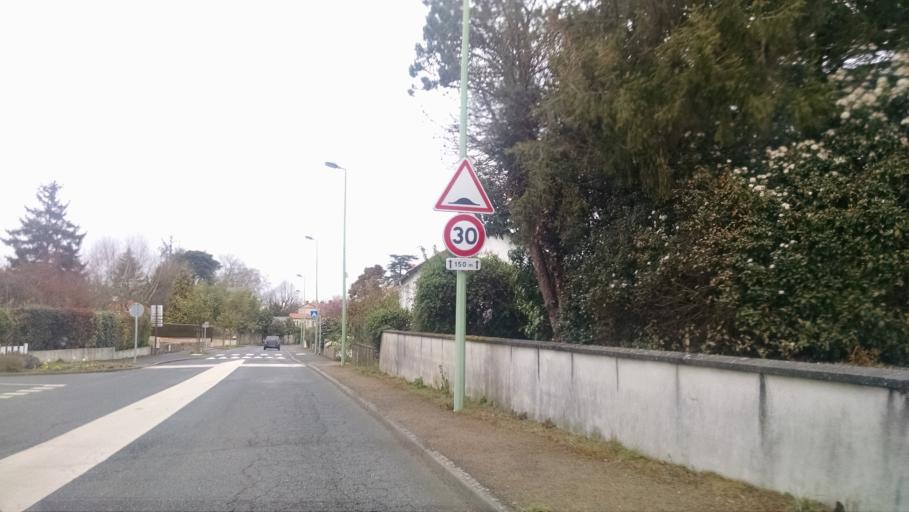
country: FR
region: Pays de la Loire
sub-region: Departement de la Loire-Atlantique
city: Monnieres
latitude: 47.1348
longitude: -1.3533
